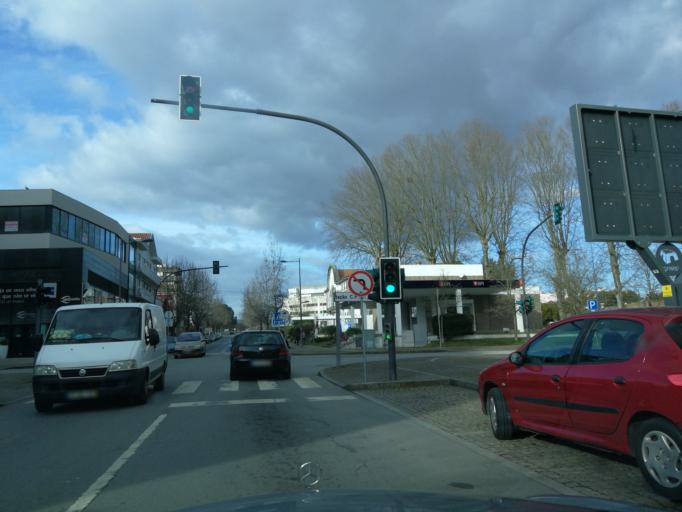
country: PT
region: Viana do Castelo
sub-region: Valenca
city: Valenza
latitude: 42.0246
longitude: -8.6413
